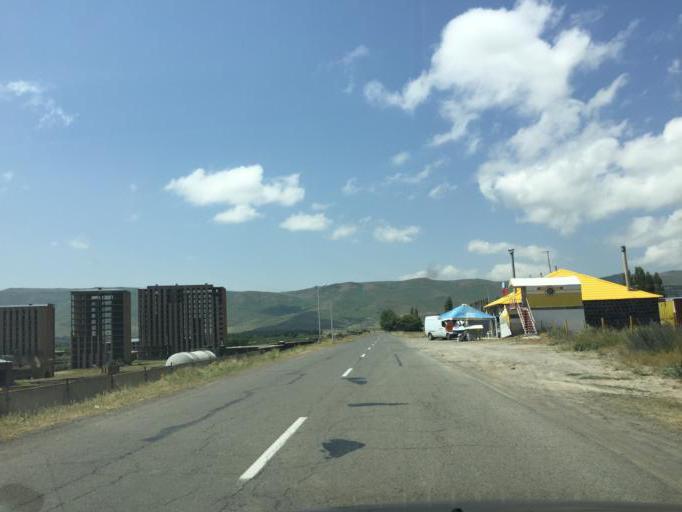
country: AM
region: Geghark'unik'i Marz
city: Tsovagyugh
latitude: 40.6282
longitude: 44.9750
